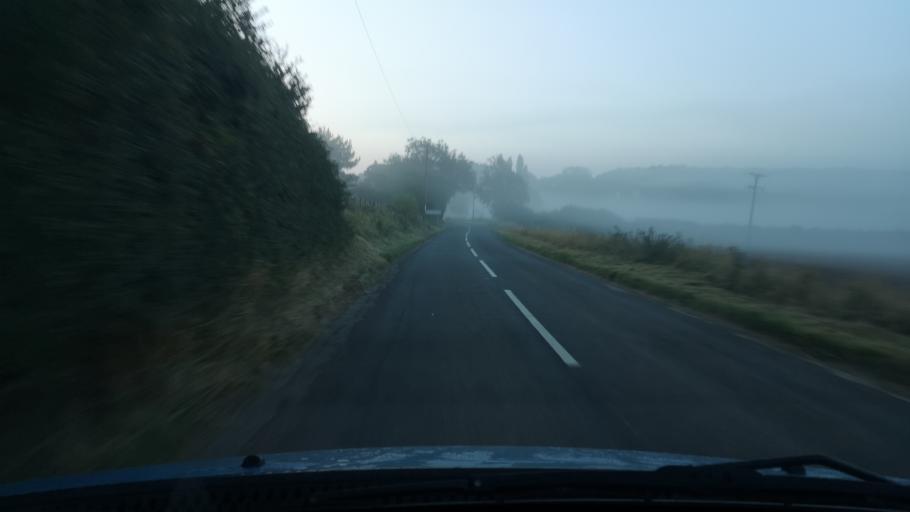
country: GB
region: England
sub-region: City and Borough of Wakefield
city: Darrington
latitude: 53.6526
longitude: -1.2677
